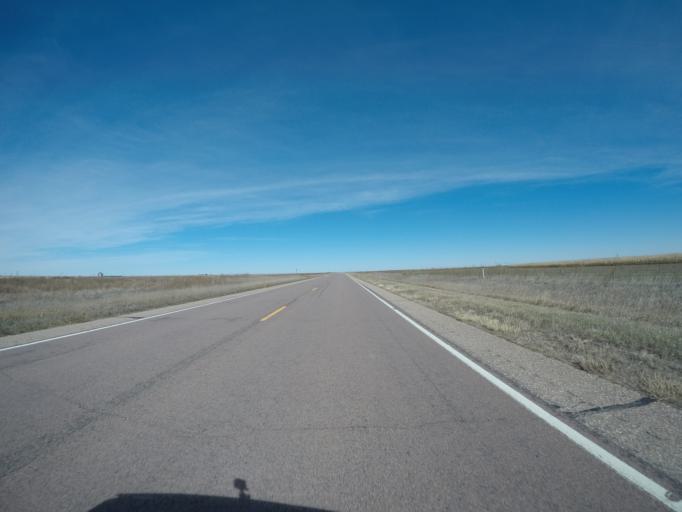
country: US
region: Colorado
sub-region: Kit Carson County
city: Burlington
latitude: 39.6784
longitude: -102.4131
